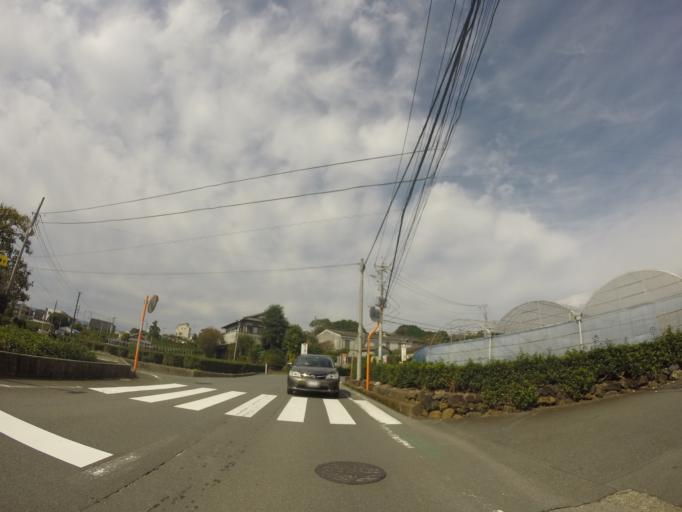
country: JP
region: Shizuoka
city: Fuji
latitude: 35.1880
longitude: 138.6924
